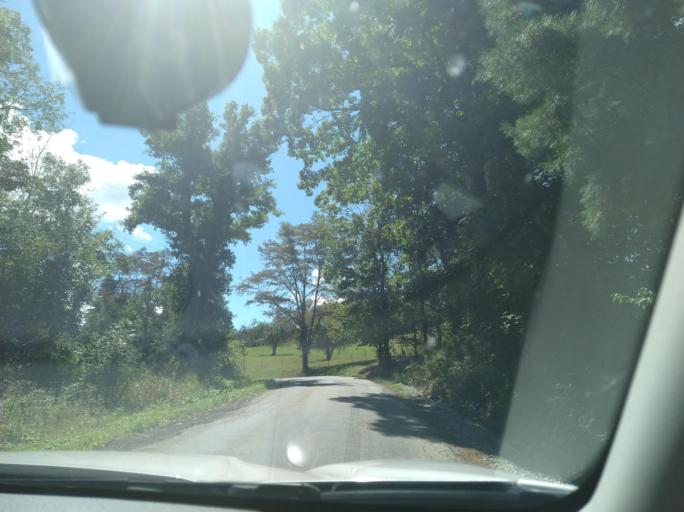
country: US
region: Pennsylvania
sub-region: Fayette County
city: Bear Rocks
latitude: 40.0985
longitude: -79.3642
